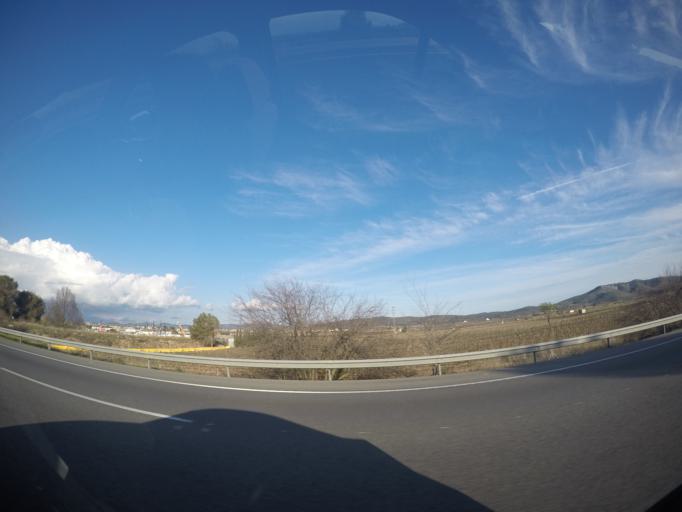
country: ES
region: Catalonia
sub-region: Provincia de Barcelona
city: Vilafranca del Penedes
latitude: 41.3460
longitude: 1.7180
